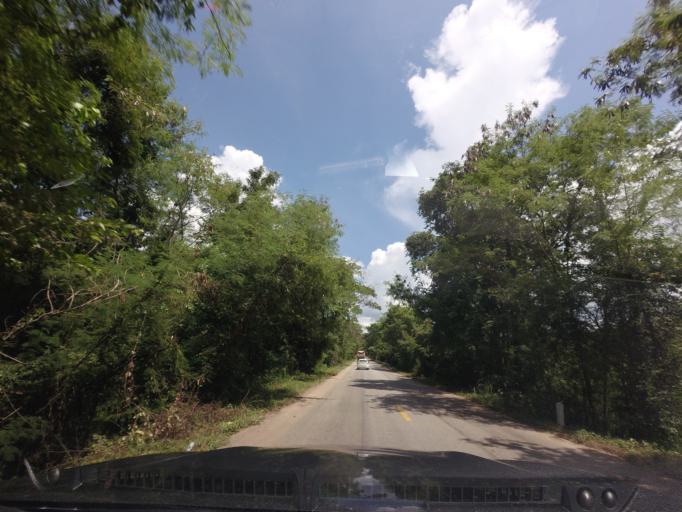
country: TH
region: Changwat Udon Thani
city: Phibun Rak
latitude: 17.5815
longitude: 103.0329
